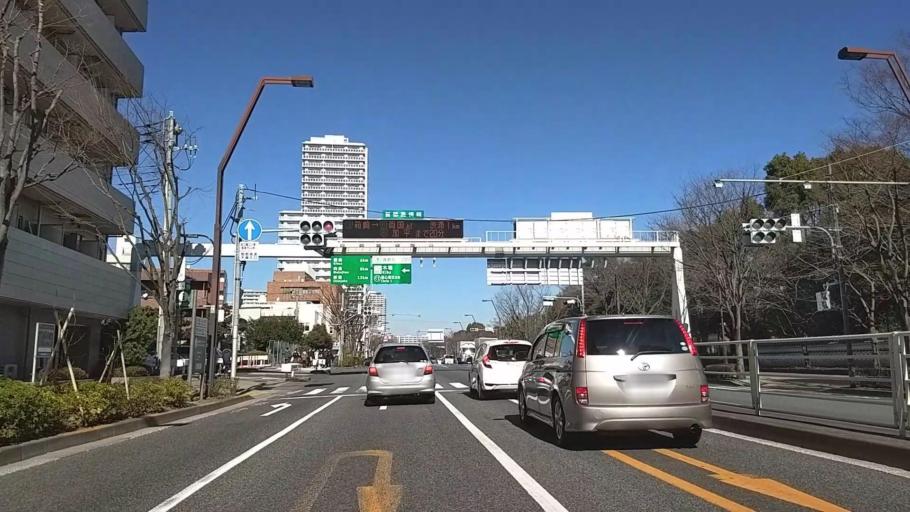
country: JP
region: Tokyo
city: Urayasu
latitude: 35.6715
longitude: 139.8062
